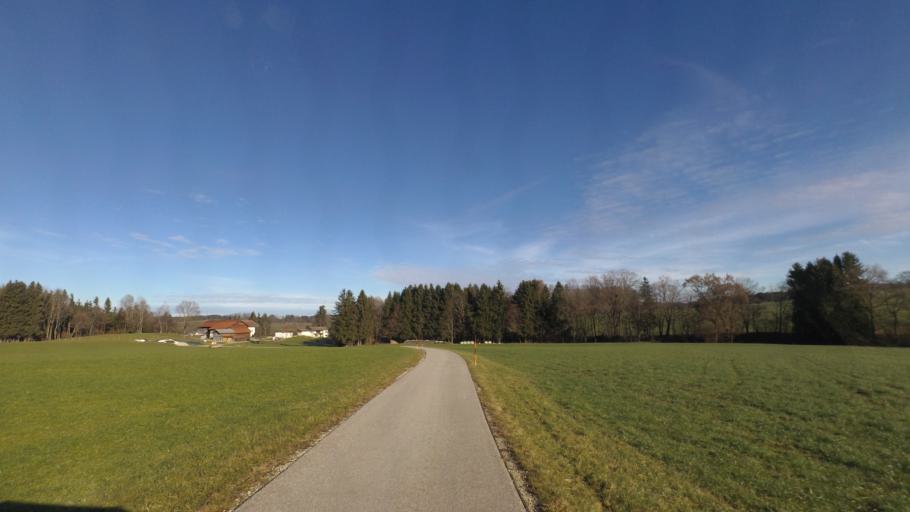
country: DE
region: Bavaria
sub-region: Upper Bavaria
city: Grabenstatt
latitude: 47.8393
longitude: 12.5760
